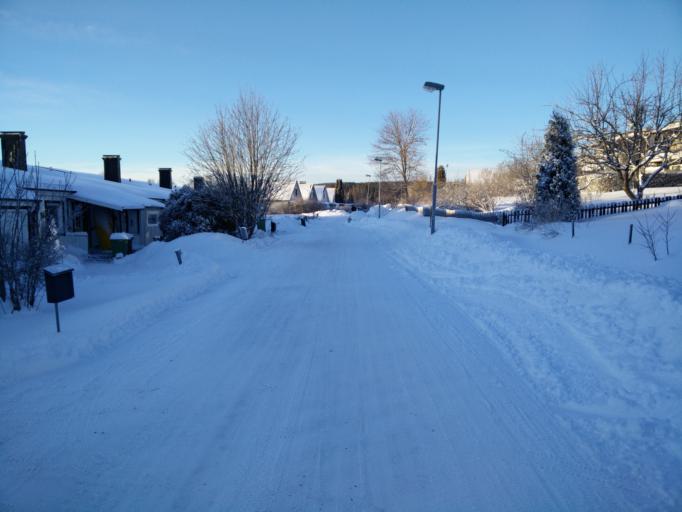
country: SE
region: Vaesternorrland
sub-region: Sundsvalls Kommun
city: Kvissleby
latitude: 62.2948
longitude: 17.3696
